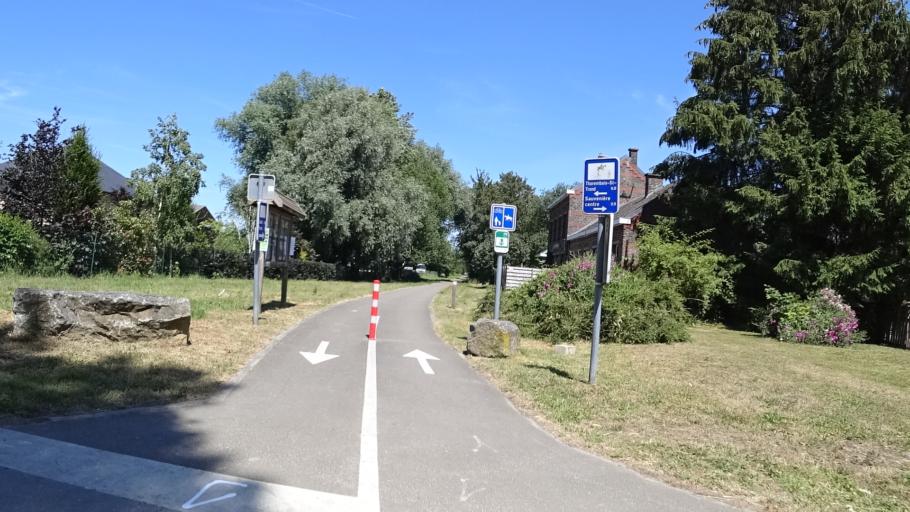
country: BE
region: Wallonia
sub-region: Province de Namur
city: Gembloux
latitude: 50.5889
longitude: 4.7225
